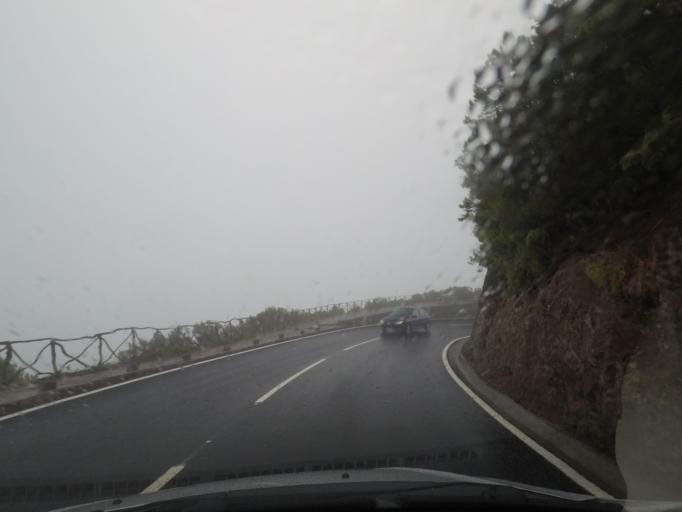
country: PT
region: Madeira
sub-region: Santana
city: Santana
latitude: 32.7708
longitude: -16.9175
